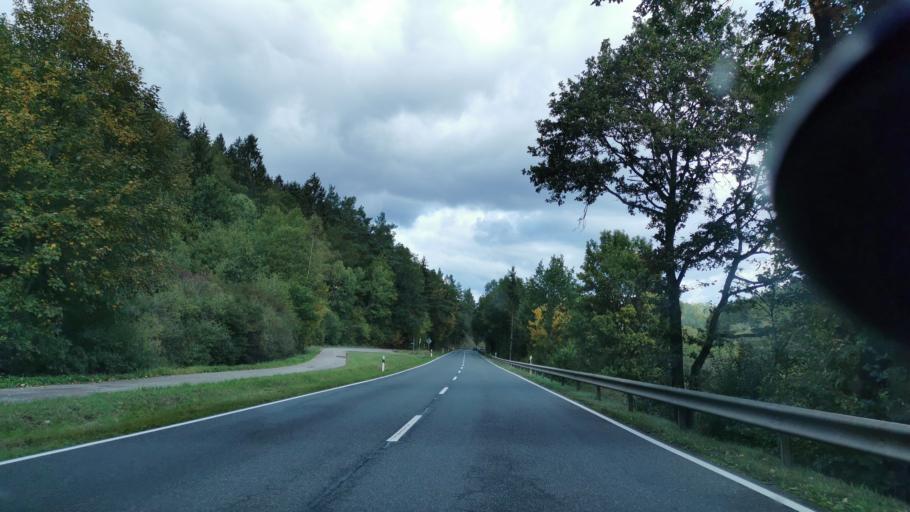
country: DE
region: Rheinland-Pfalz
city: Uxheim
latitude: 50.3616
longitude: 6.7756
